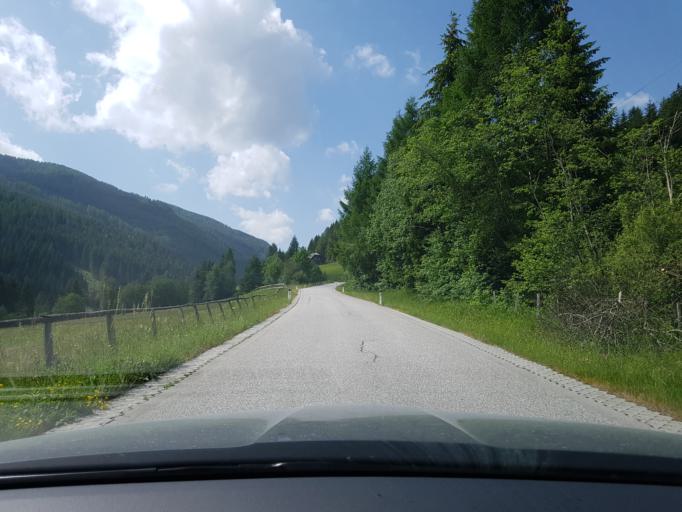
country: AT
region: Salzburg
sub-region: Politischer Bezirk Tamsweg
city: Thomatal
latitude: 47.0737
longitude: 13.7240
